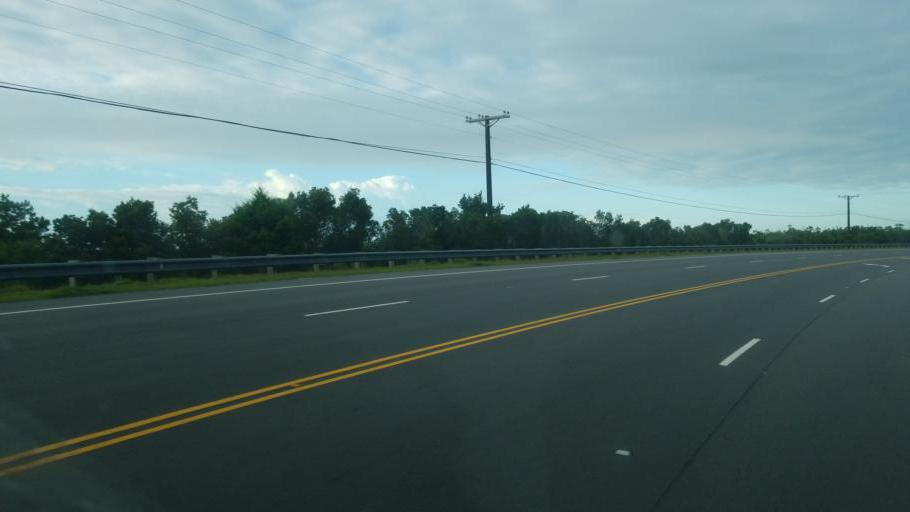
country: US
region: North Carolina
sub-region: Dare County
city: Manteo
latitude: 35.8732
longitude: -75.7825
